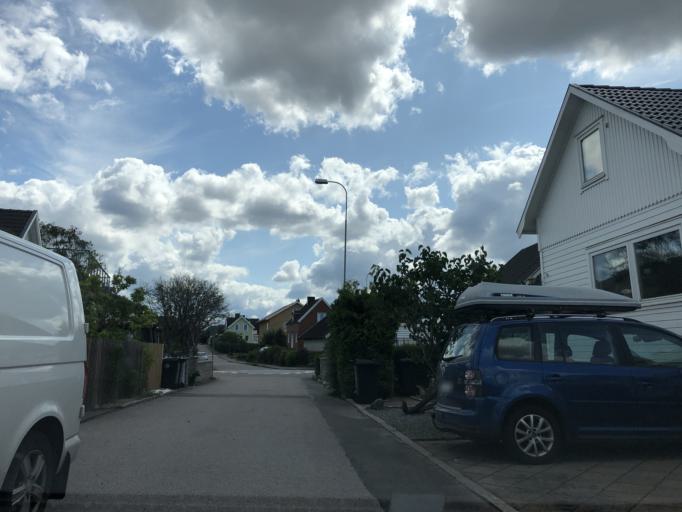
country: SE
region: Vaestra Goetaland
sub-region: Goteborg
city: Majorna
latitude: 57.7201
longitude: 11.9095
